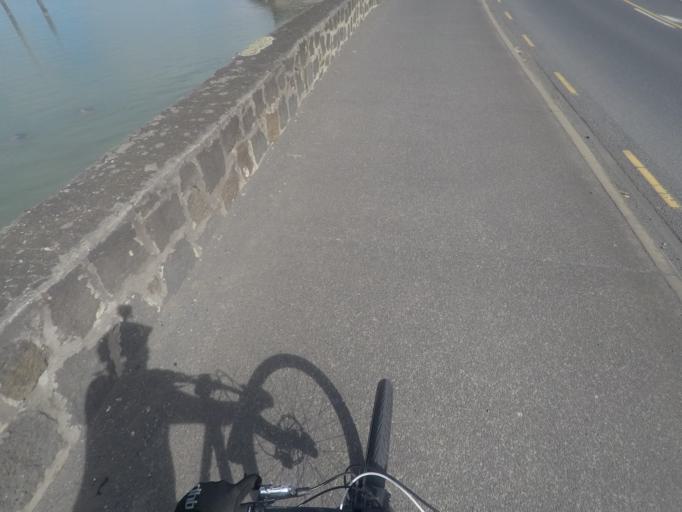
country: NZ
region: Auckland
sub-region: Auckland
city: Mangere
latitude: -36.9312
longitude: 174.7826
